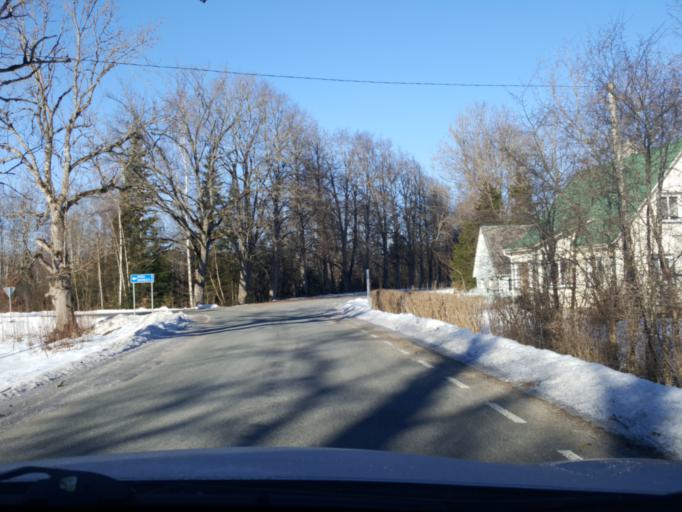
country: EE
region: Viljandimaa
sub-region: Viljandi linn
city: Viljandi
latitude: 58.4192
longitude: 25.5414
